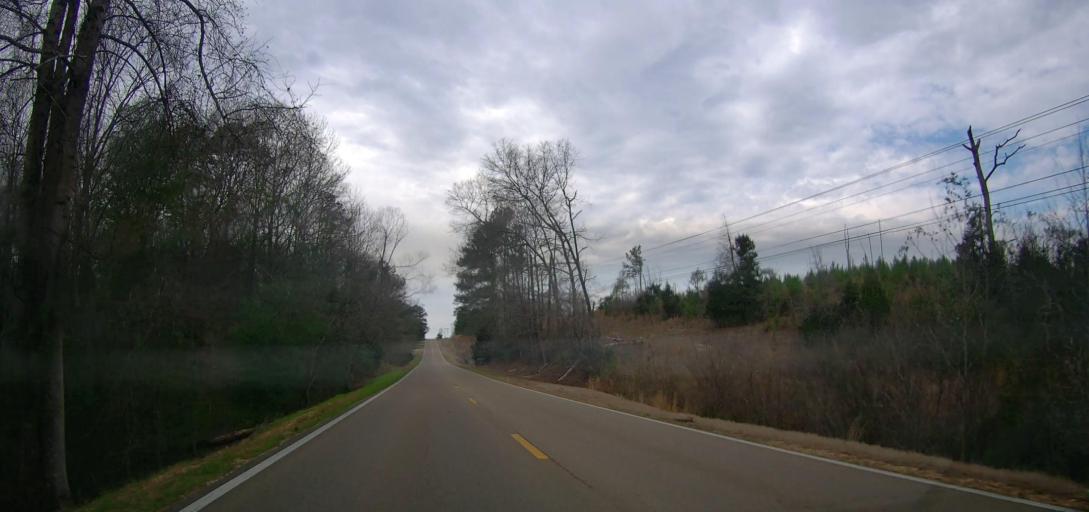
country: US
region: Mississippi
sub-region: Itawamba County
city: Fulton
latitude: 34.2755
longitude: -88.3522
